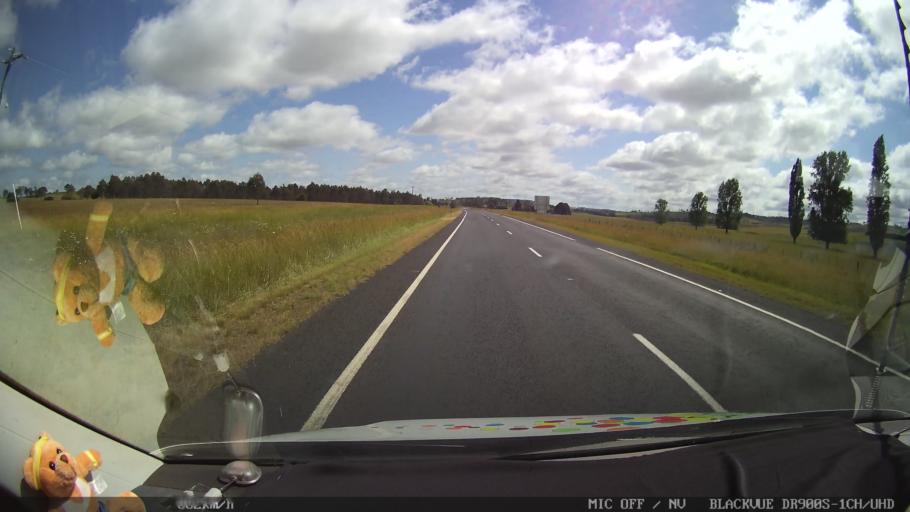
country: AU
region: New South Wales
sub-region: Glen Innes Severn
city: Glen Innes
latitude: -29.9175
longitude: 151.7272
